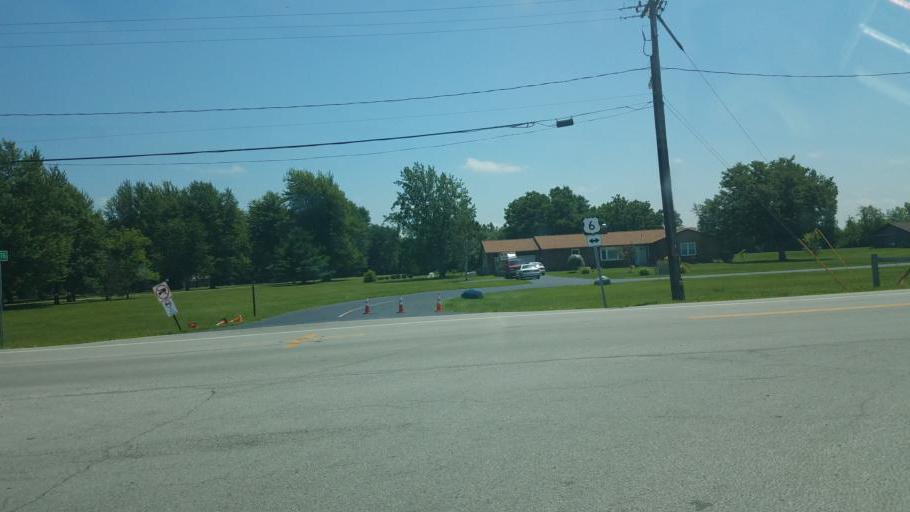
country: US
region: Ohio
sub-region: Sandusky County
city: Fremont
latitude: 41.3653
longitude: -83.0821
